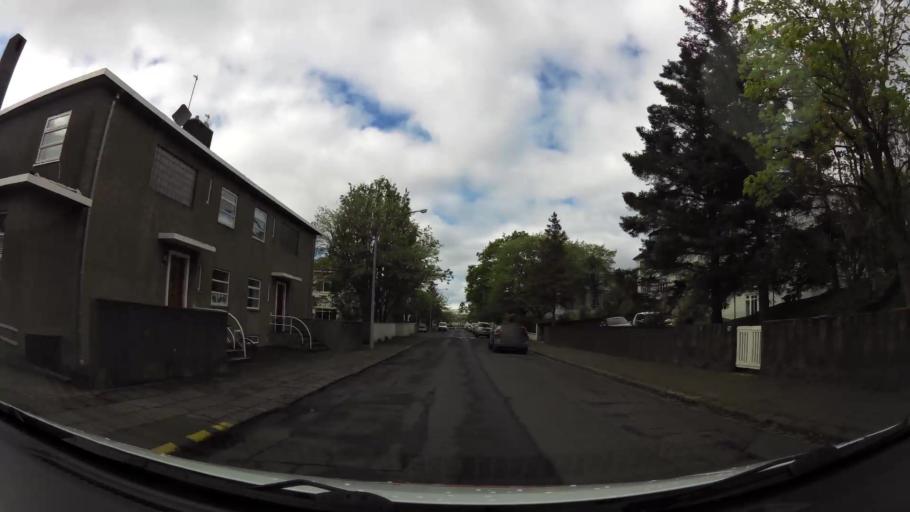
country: IS
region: Capital Region
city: Kopavogur
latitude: 64.1398
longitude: -21.9340
